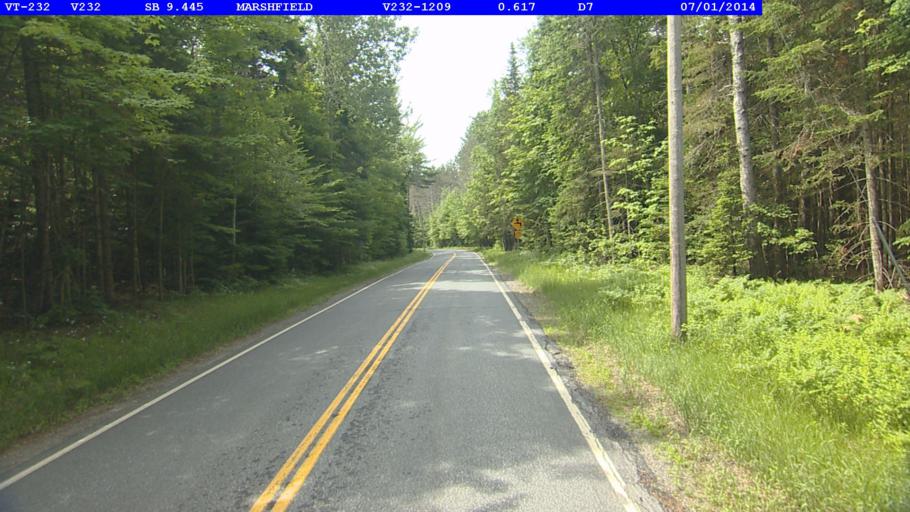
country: US
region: Vermont
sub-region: Caledonia County
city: Hardwick
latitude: 44.3248
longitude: -72.2895
